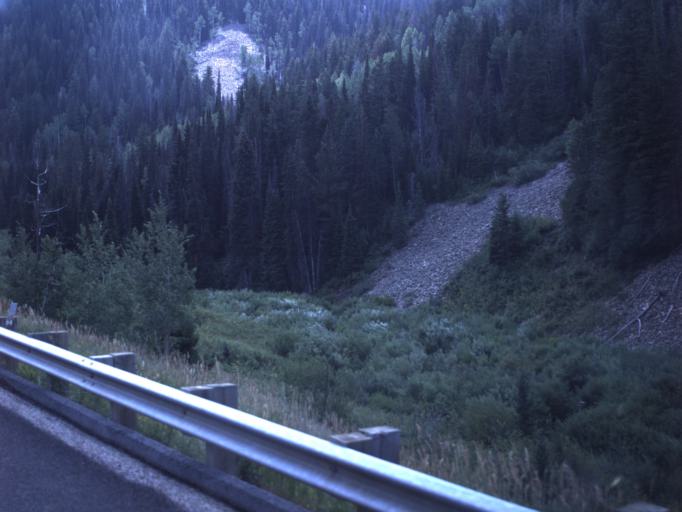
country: US
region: Utah
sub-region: Summit County
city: Francis
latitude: 40.5242
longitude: -111.0920
